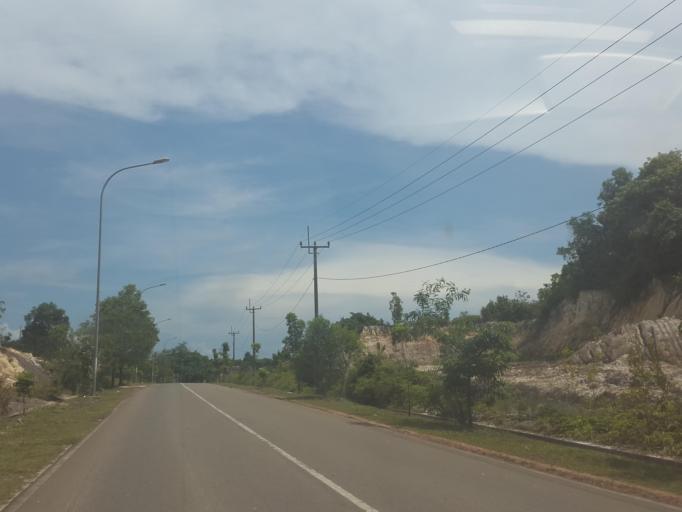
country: SG
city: Singapore
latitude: 0.9618
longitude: 104.0553
